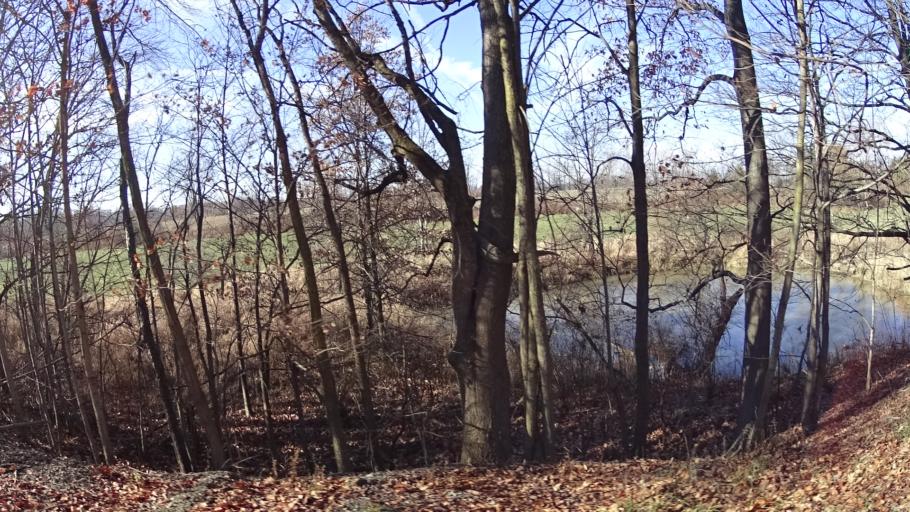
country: US
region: Ohio
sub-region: Lorain County
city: Wellington
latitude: 41.0693
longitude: -82.2796
